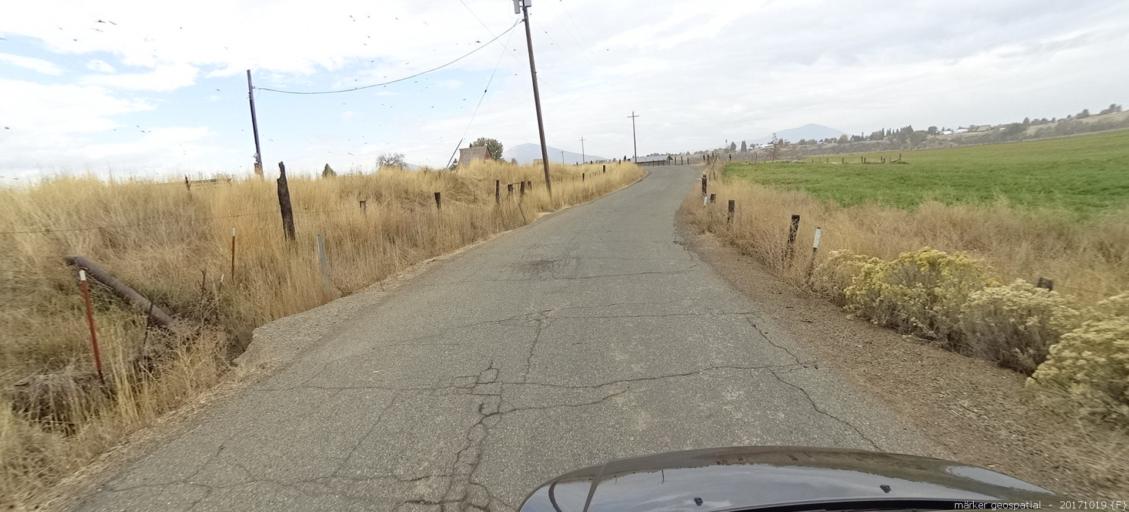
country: US
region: California
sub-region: Shasta County
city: Burney
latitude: 41.0444
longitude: -121.3805
